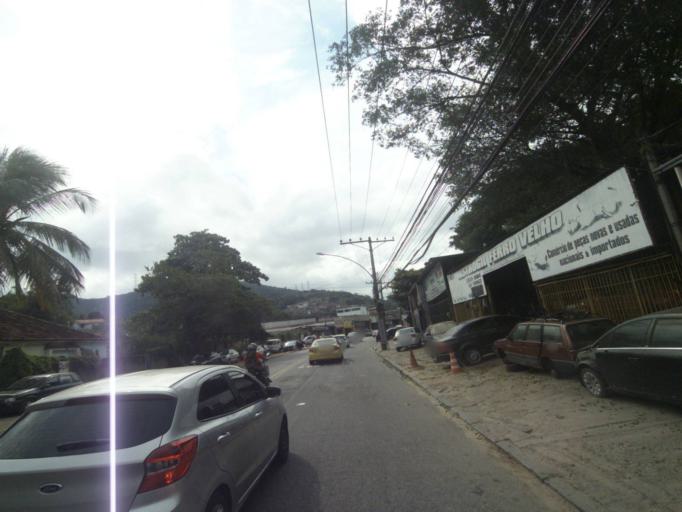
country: BR
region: Rio de Janeiro
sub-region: Sao Joao De Meriti
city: Sao Joao de Meriti
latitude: -22.9107
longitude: -43.3782
